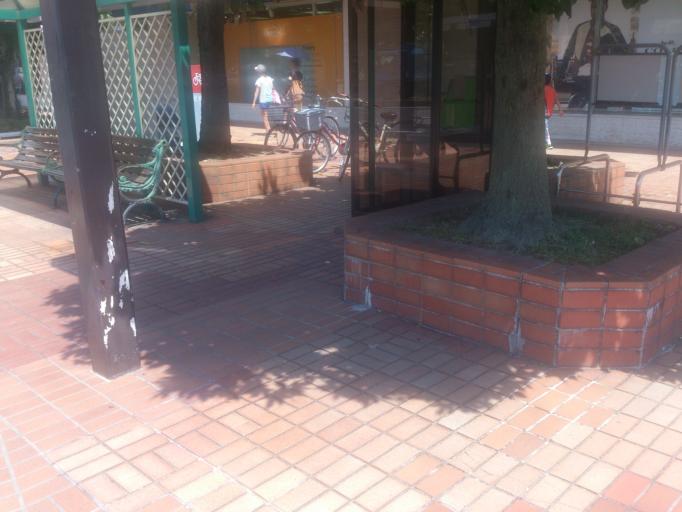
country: JP
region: Shiga Prefecture
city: Otsu-shi
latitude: 35.0036
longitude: 135.8820
